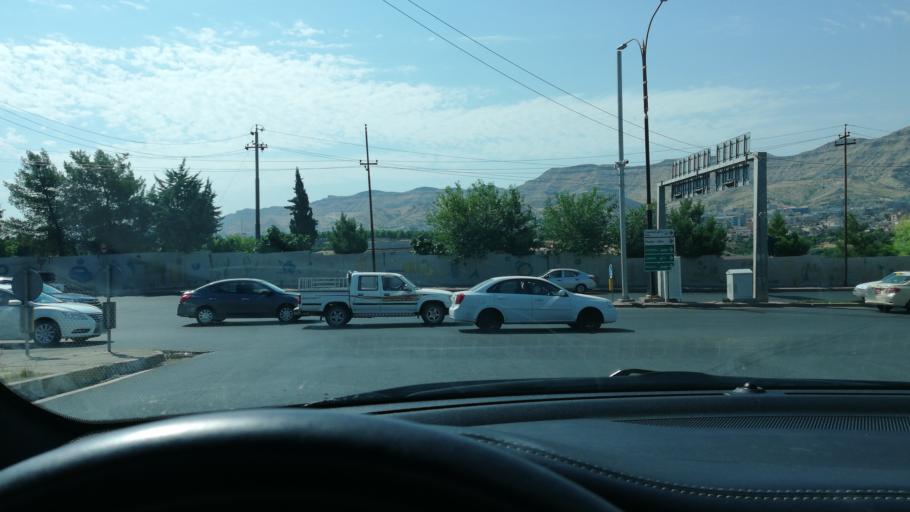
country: IQ
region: Dahuk
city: Dihok
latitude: 36.8609
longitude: 42.9848
